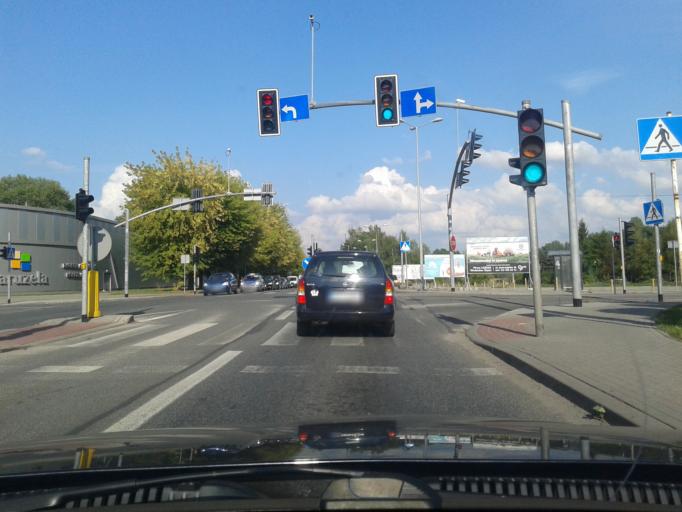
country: PL
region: Silesian Voivodeship
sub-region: Powiat wodzislawski
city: Wodzislaw Slaski
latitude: 49.9996
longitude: 18.4640
